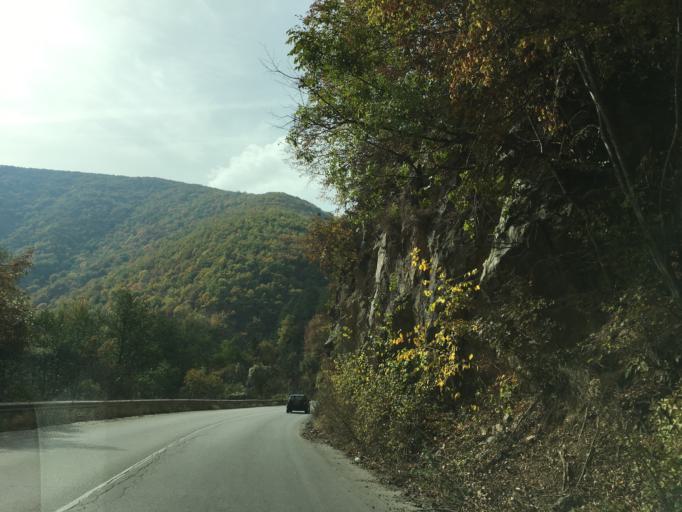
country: BG
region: Sofia-Capital
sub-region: Stolichna Obshtina
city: Sofia
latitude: 42.5621
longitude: 23.4240
